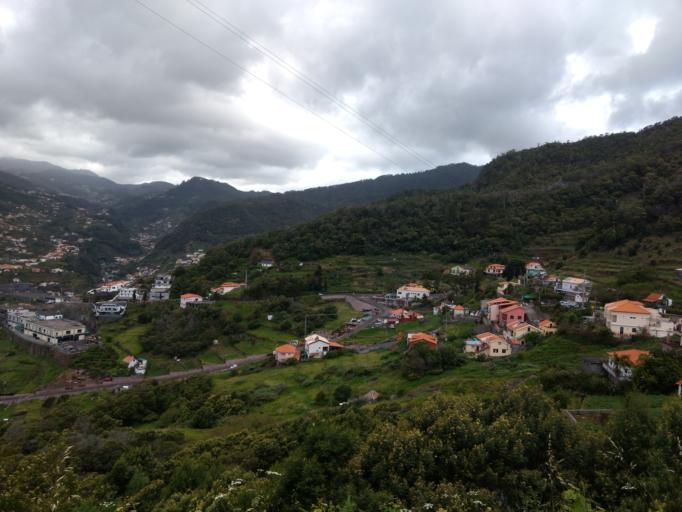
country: PT
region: Madeira
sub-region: Machico
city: Canical
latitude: 32.7310
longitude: -16.7631
